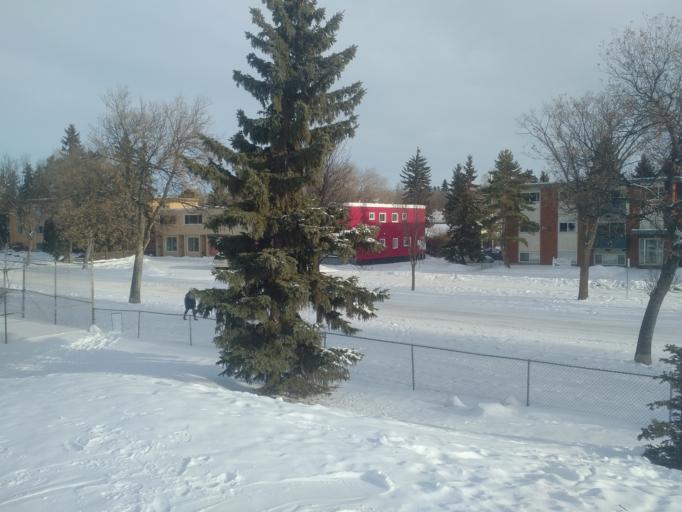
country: CA
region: Alberta
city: Edmonton
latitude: 53.5032
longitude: -113.5170
